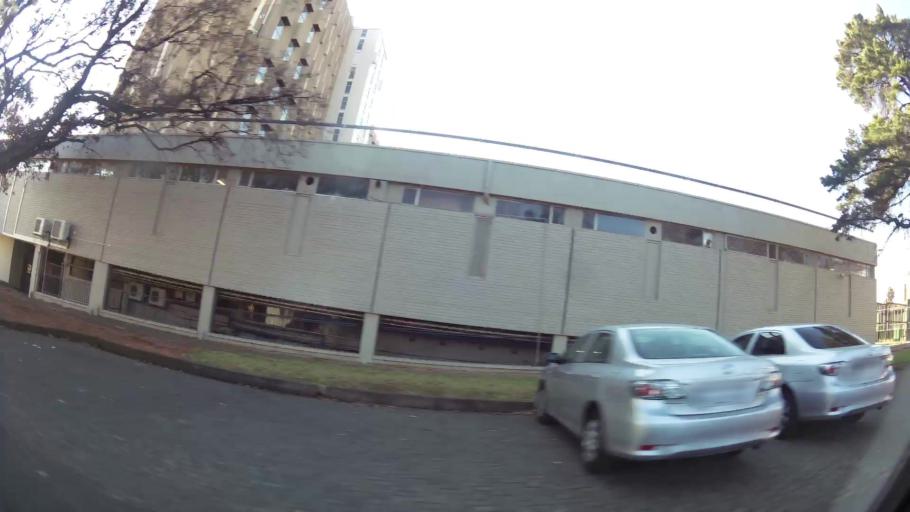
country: ZA
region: Gauteng
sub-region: Ekurhuleni Metropolitan Municipality
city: Germiston
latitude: -26.1964
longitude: 28.1197
